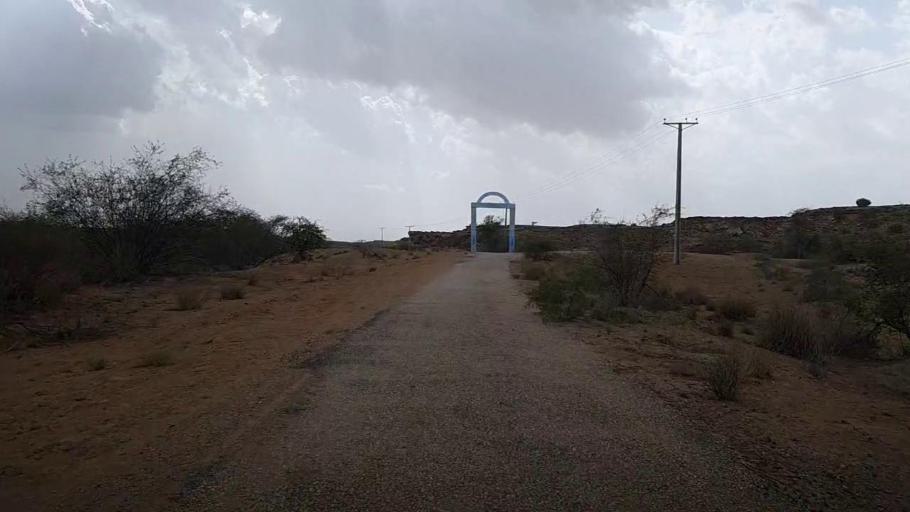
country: PK
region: Sindh
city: Jamshoro
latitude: 25.3934
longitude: 67.6862
